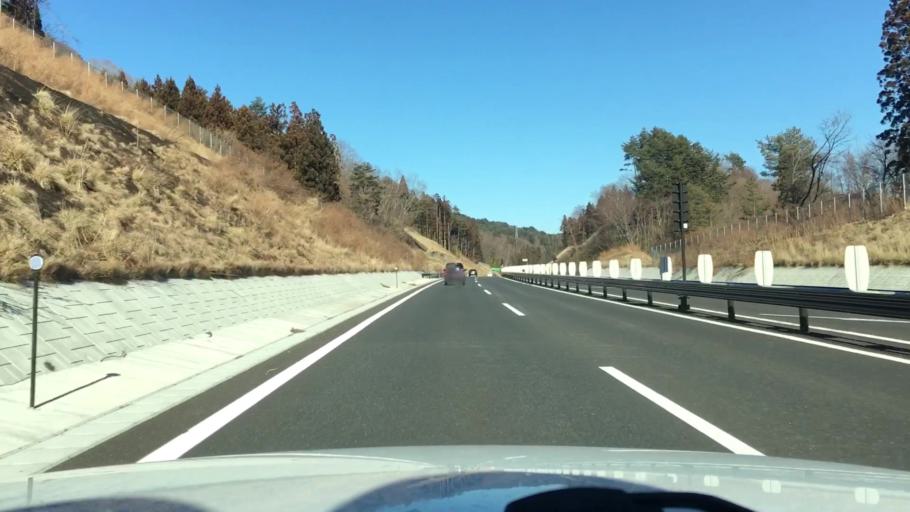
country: JP
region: Iwate
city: Miyako
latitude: 39.5759
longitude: 141.9283
